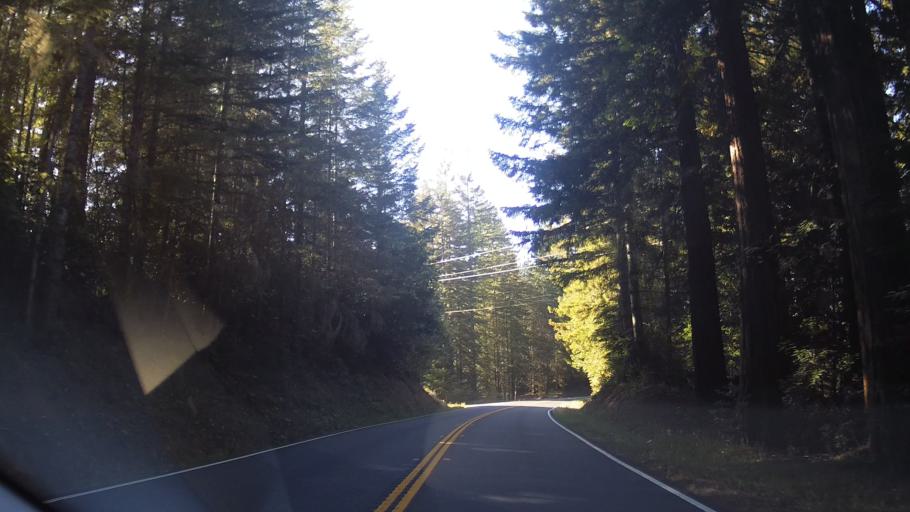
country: US
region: California
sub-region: Mendocino County
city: Fort Bragg
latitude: 39.3804
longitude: -123.6917
